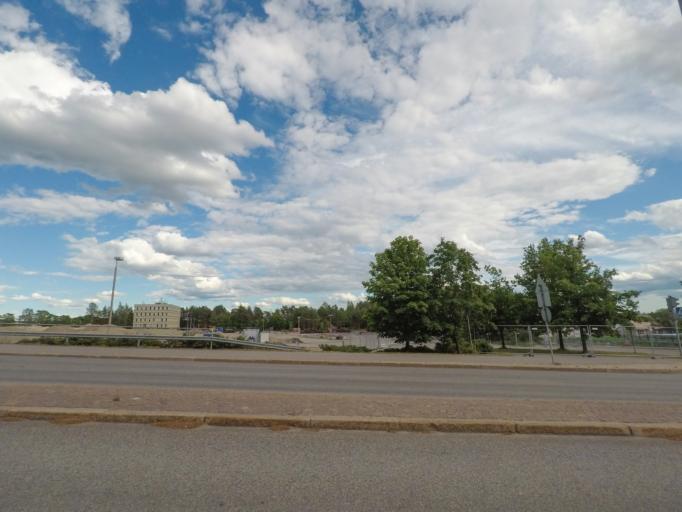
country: FI
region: Paijanne Tavastia
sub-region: Lahti
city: Lahti
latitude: 60.9751
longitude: 25.6376
